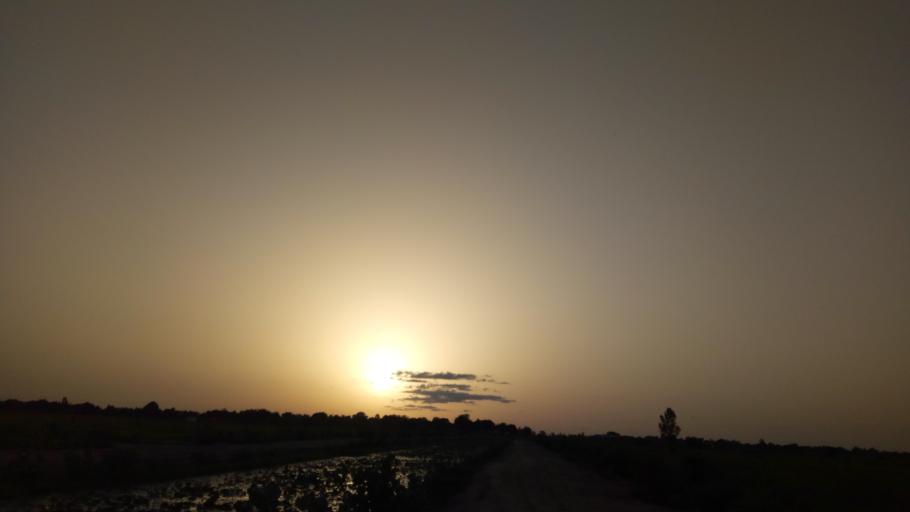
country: ML
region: Segou
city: Niono
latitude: 14.3146
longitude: -5.9465
